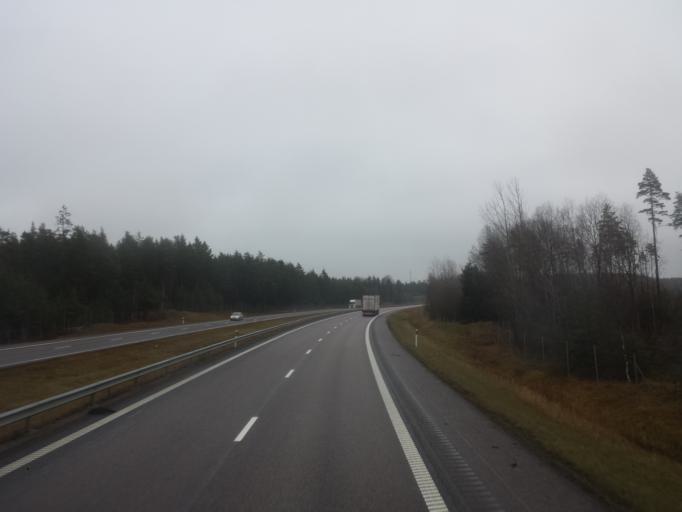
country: SE
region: Soedermanland
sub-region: Nykopings Kommun
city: Svalsta
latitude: 58.7517
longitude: 16.9006
